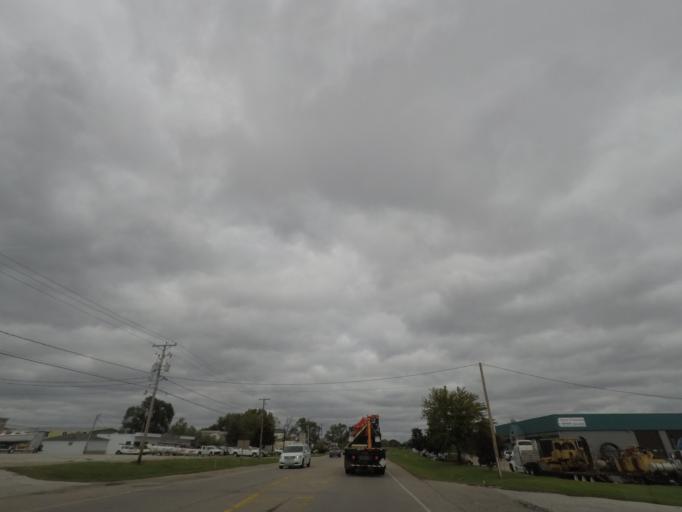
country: US
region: Iowa
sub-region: Polk County
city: Saylorville
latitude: 41.6594
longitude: -93.6005
